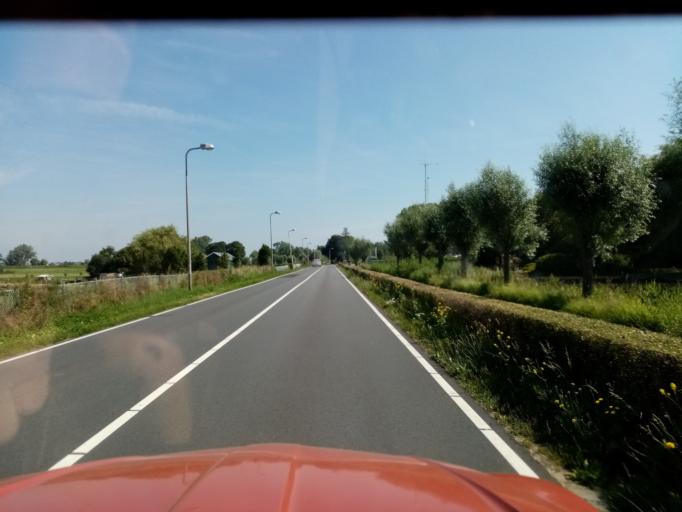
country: NL
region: South Holland
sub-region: Gemeente Kaag en Braassem
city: Leimuiden
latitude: 52.1792
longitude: 4.7072
